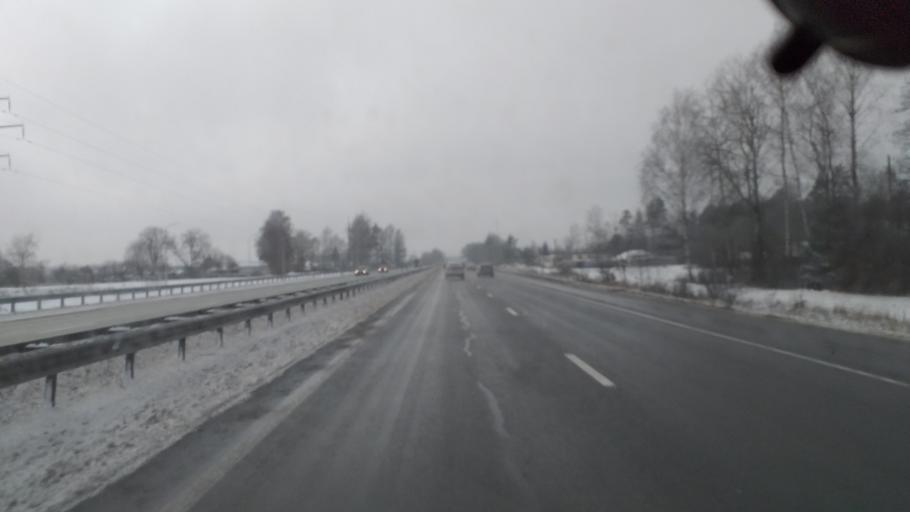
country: LV
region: Marupe
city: Marupe
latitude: 56.8242
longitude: 24.0245
